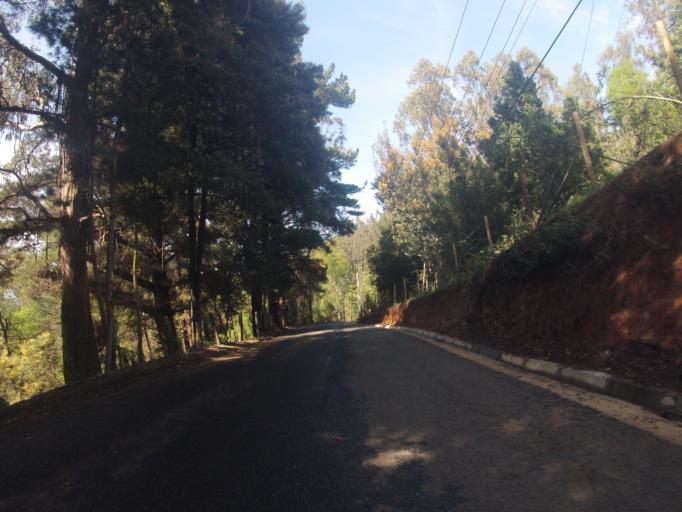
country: CL
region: Araucania
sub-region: Provincia de Cautin
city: Temuco
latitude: -38.6882
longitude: -72.5571
